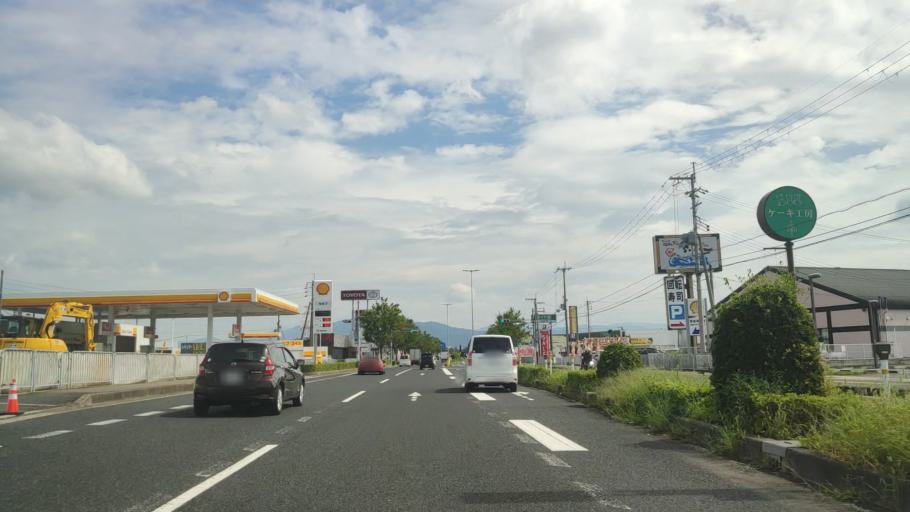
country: JP
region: Wakayama
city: Iwade
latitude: 34.2633
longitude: 135.2886
